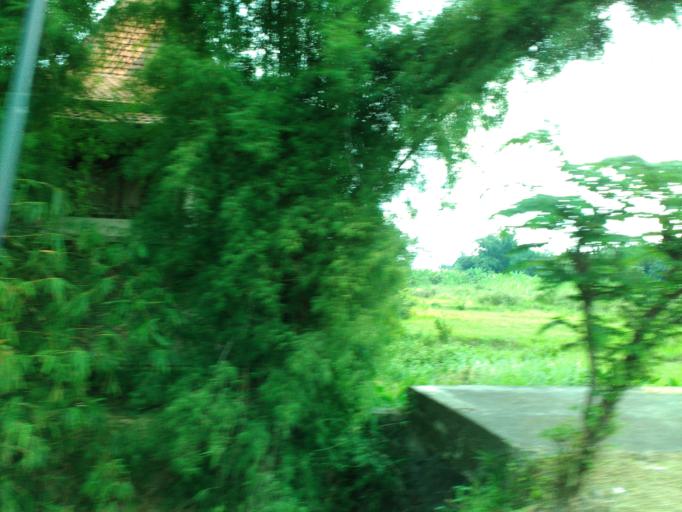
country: ID
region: Central Java
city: Ceper
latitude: -7.6667
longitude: 110.6627
